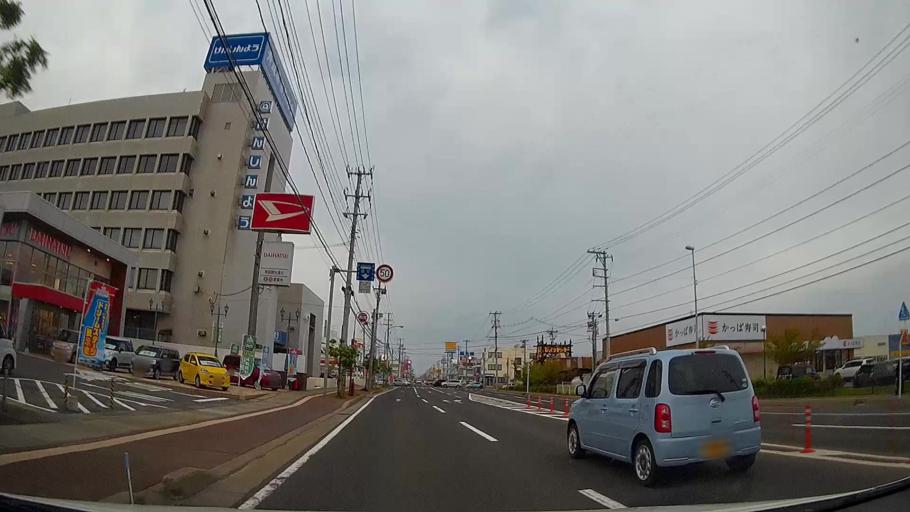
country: JP
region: Aomori
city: Aomori Shi
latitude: 40.7988
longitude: 140.7577
